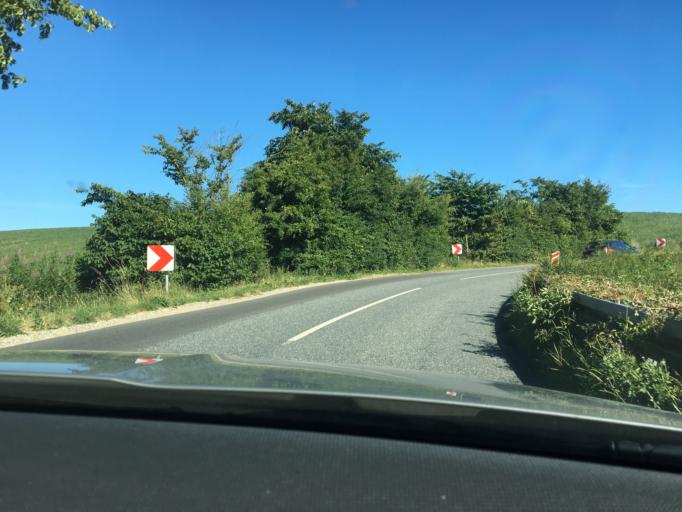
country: DK
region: Central Jutland
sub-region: Syddjurs Kommune
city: Hornslet
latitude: 56.3095
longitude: 10.3429
